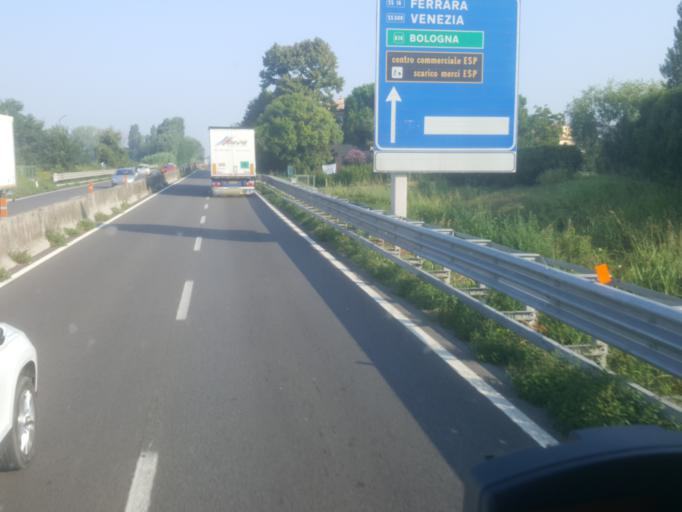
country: IT
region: Emilia-Romagna
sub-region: Provincia di Ravenna
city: Ravenna
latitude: 44.4031
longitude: 12.1781
